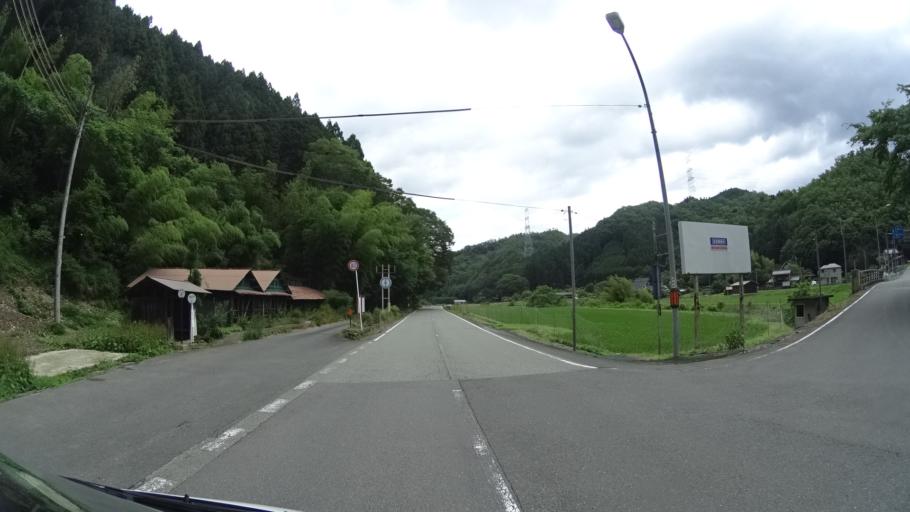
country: JP
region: Kyoto
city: Kameoka
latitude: 35.0686
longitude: 135.4074
